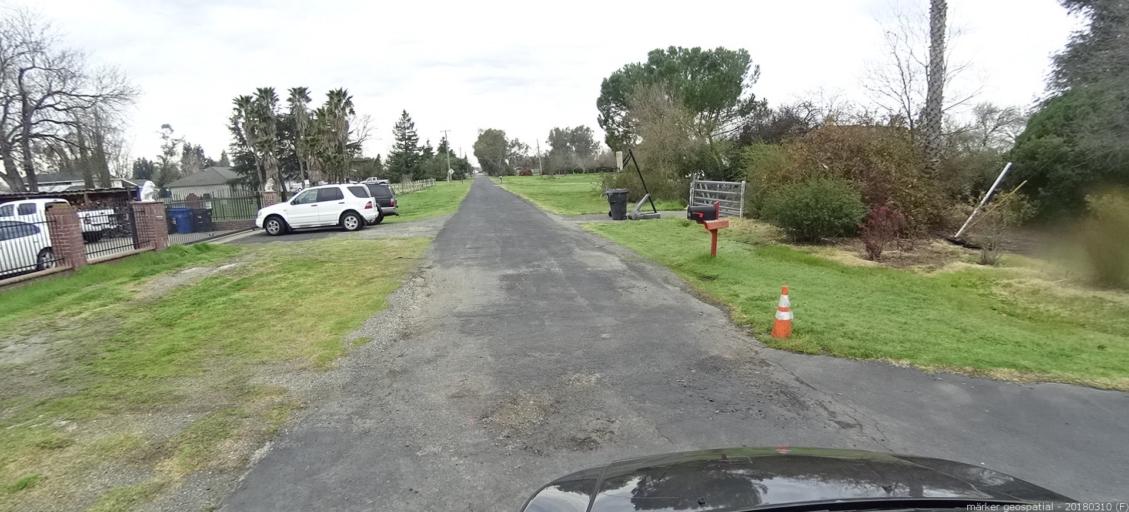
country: US
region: California
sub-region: Sacramento County
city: Vineyard
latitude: 38.4753
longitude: -121.3630
